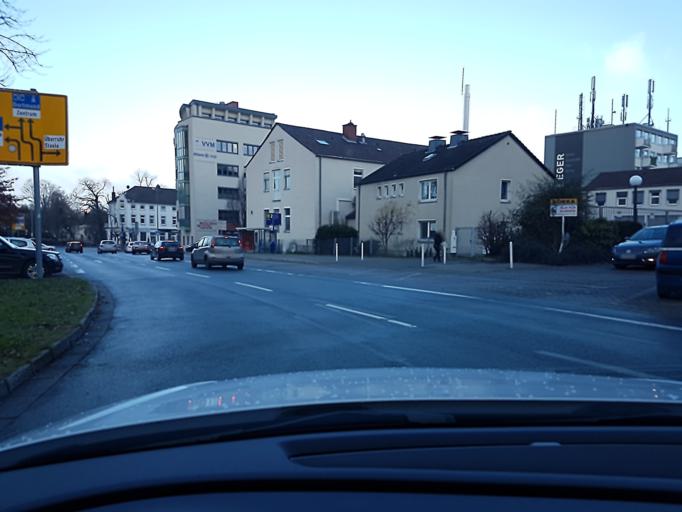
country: DE
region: North Rhine-Westphalia
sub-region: Regierungsbezirk Dusseldorf
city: Essen
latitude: 51.4188
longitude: 7.0247
